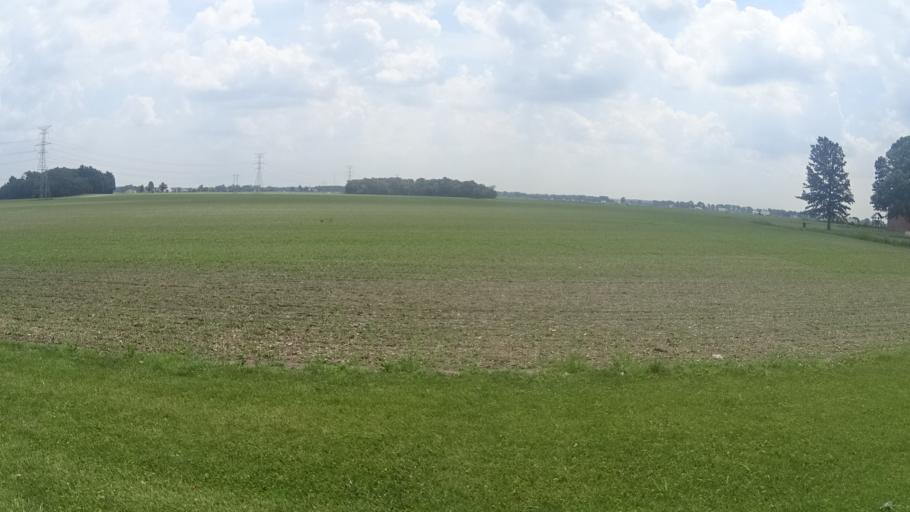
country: US
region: Ohio
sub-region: Erie County
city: Milan
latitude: 41.3359
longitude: -82.6733
